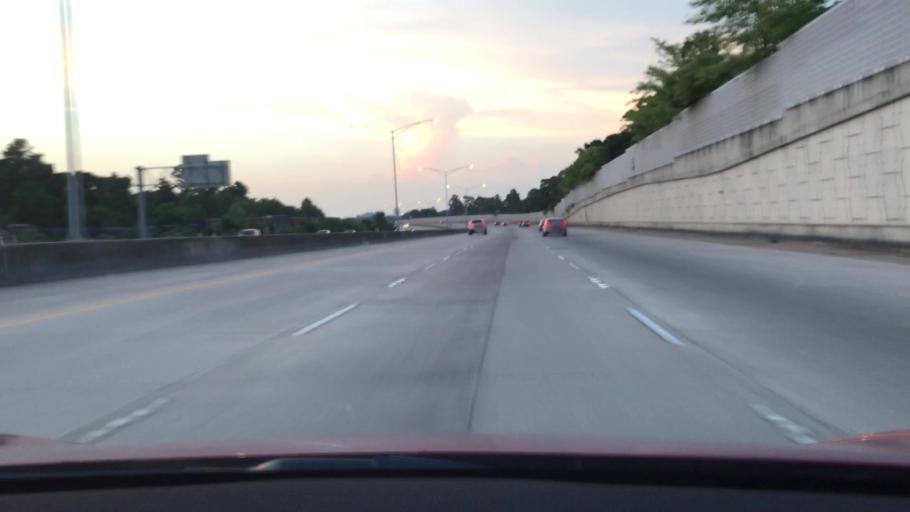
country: US
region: Louisiana
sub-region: Bossier Parish
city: Bossier City
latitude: 32.4635
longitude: -93.7562
